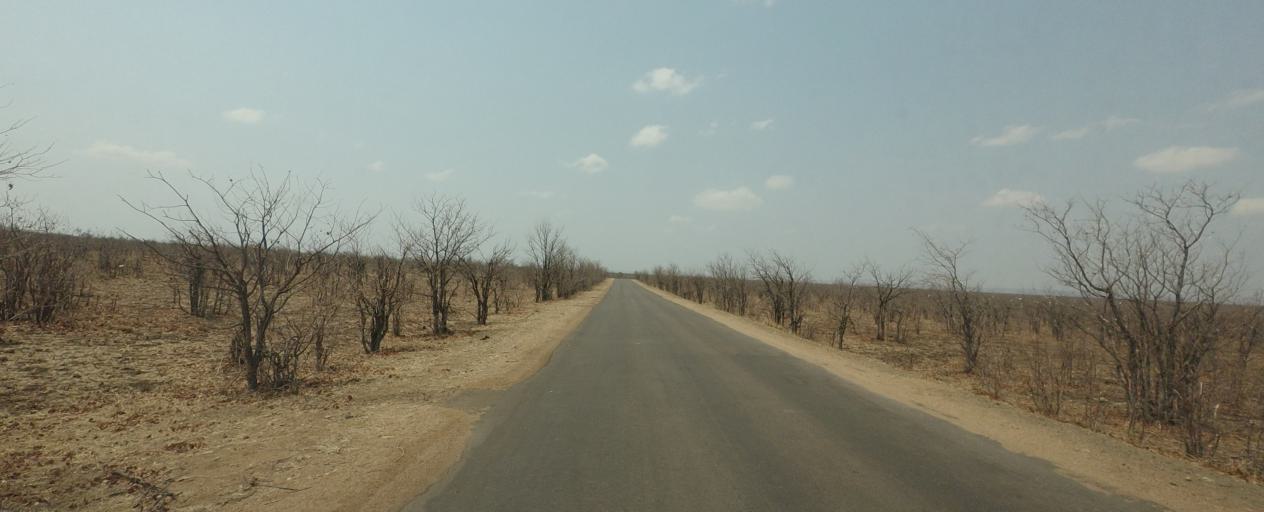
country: ZA
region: Limpopo
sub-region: Mopani District Municipality
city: Phalaborwa
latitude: -23.5182
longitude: 31.4056
